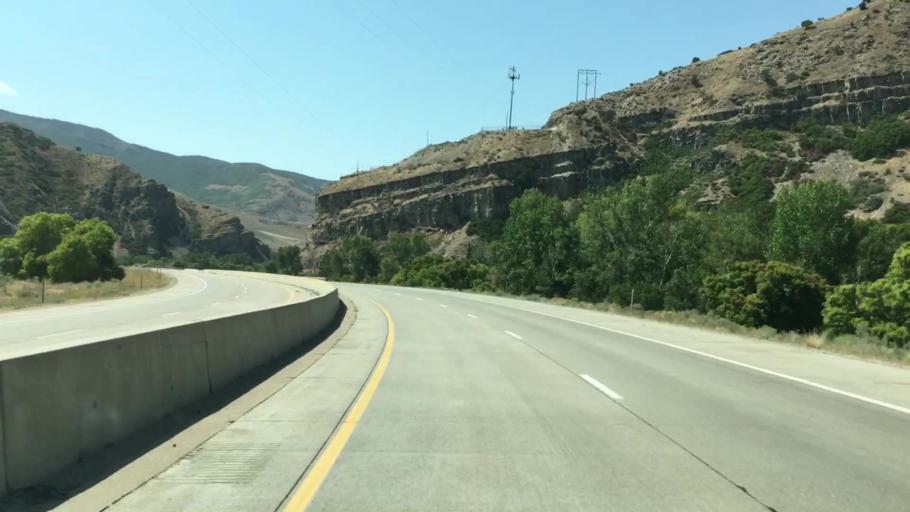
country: US
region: Utah
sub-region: Morgan County
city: Morgan
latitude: 41.0526
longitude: -111.6026
